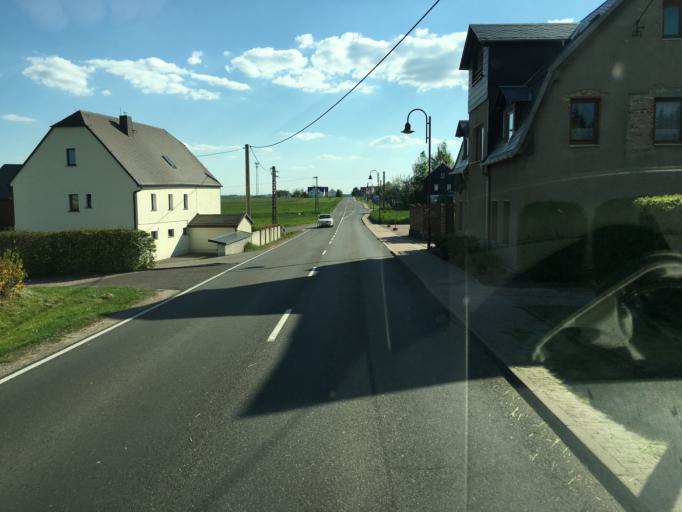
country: DE
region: Saxony
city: Hainichen
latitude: 51.0006
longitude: 13.1262
